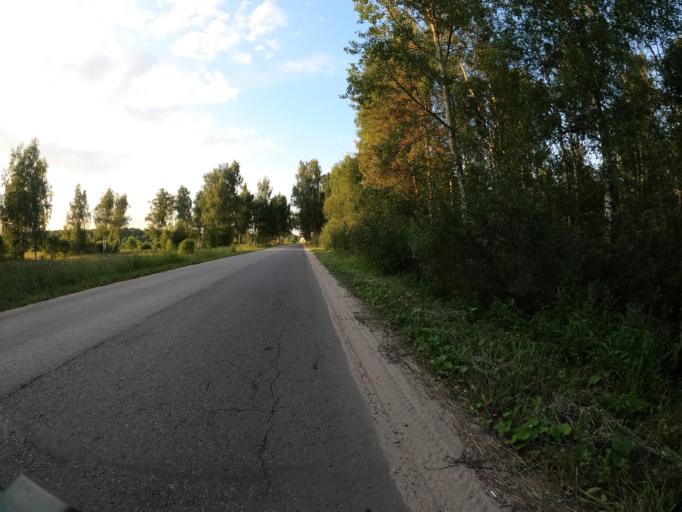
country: RU
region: Moskovskaya
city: Malyshevo
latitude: 55.5226
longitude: 38.2966
